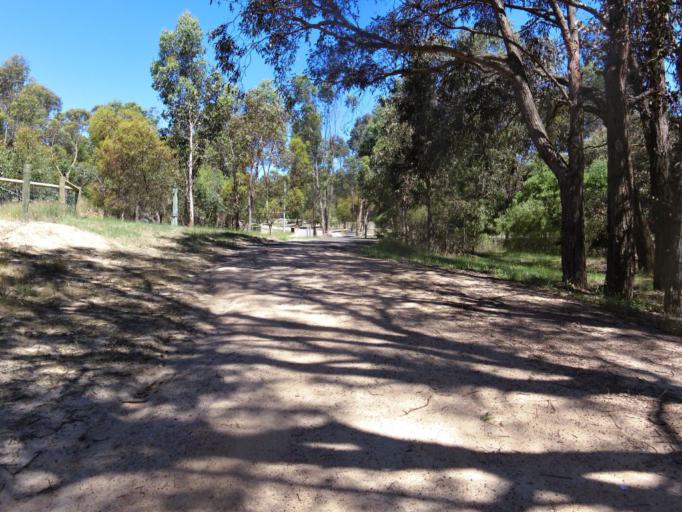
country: AU
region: Victoria
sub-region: Whittlesea
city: Whittlesea
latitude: -37.3668
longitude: 145.0369
